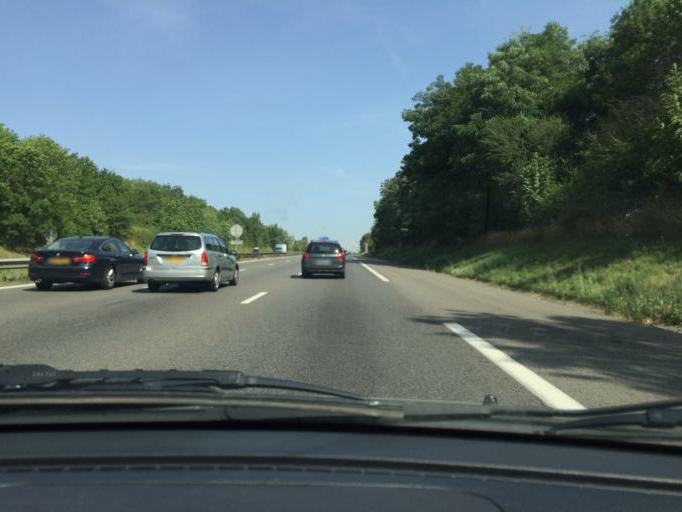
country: FR
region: Rhone-Alpes
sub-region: Departement du Rhone
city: Ecully
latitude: 45.7976
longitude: 4.7772
